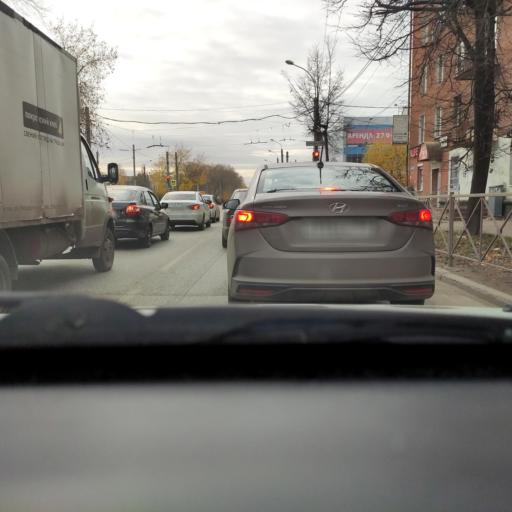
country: RU
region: Perm
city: Perm
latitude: 57.9664
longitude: 56.2447
